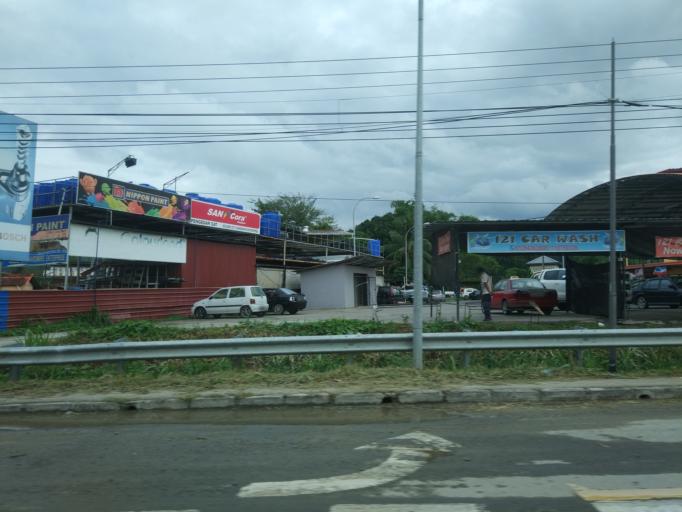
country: MY
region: Sabah
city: Kota Kinabalu
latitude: 6.0914
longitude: 116.1968
